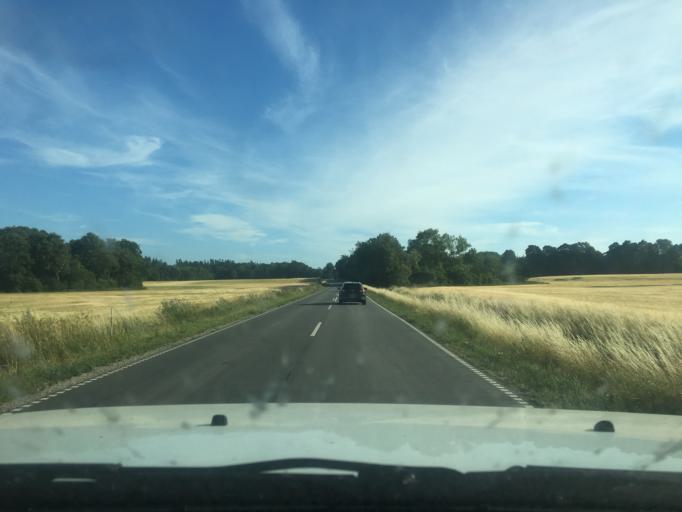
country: DK
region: Central Jutland
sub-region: Syddjurs Kommune
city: Hornslet
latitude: 56.3390
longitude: 10.3366
